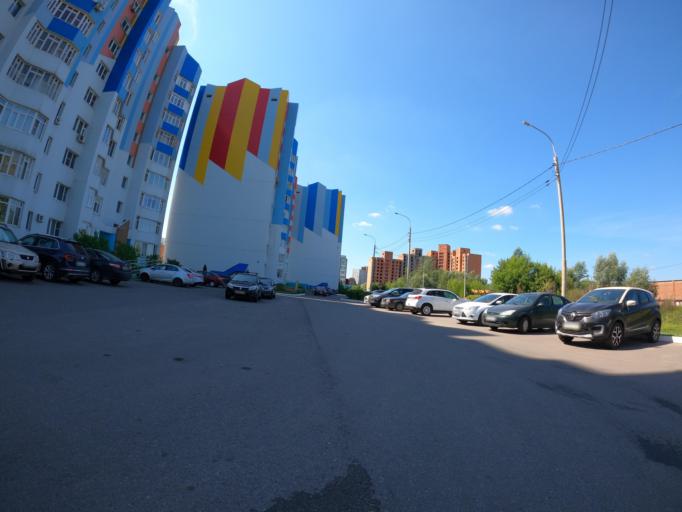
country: RU
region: Moskovskaya
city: Stupino
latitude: 54.8952
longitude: 38.0692
